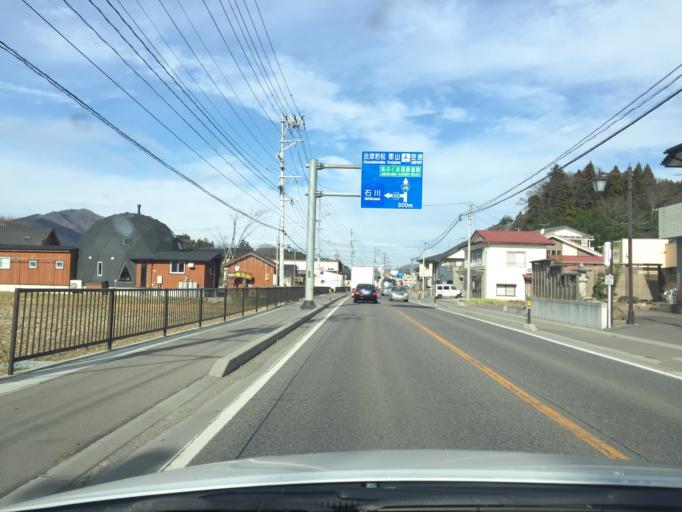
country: JP
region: Fukushima
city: Ishikawa
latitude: 37.2372
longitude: 140.5707
